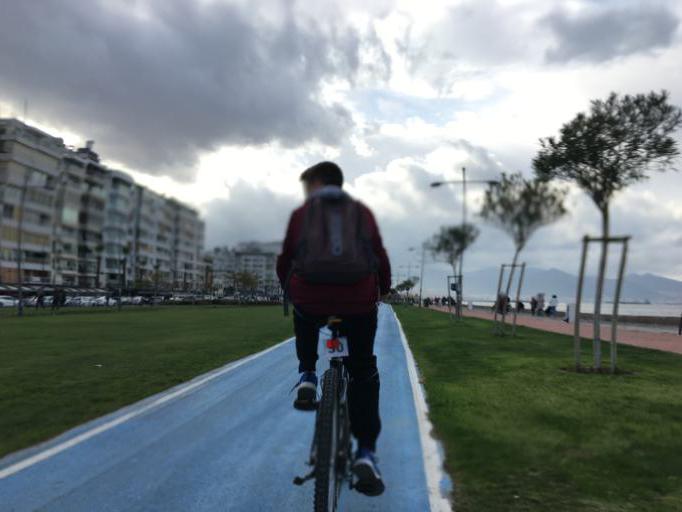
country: TR
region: Izmir
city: Izmir
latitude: 38.4350
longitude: 27.1387
